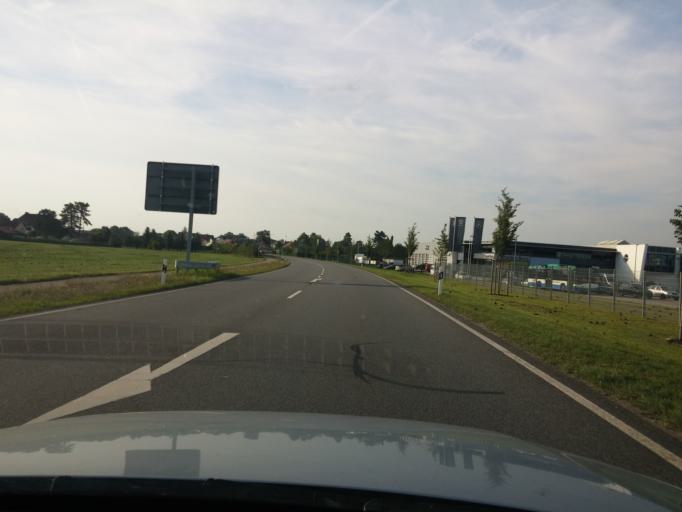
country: DE
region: Bavaria
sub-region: Upper Bavaria
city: Feldkirchen
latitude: 48.1403
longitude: 11.7359
